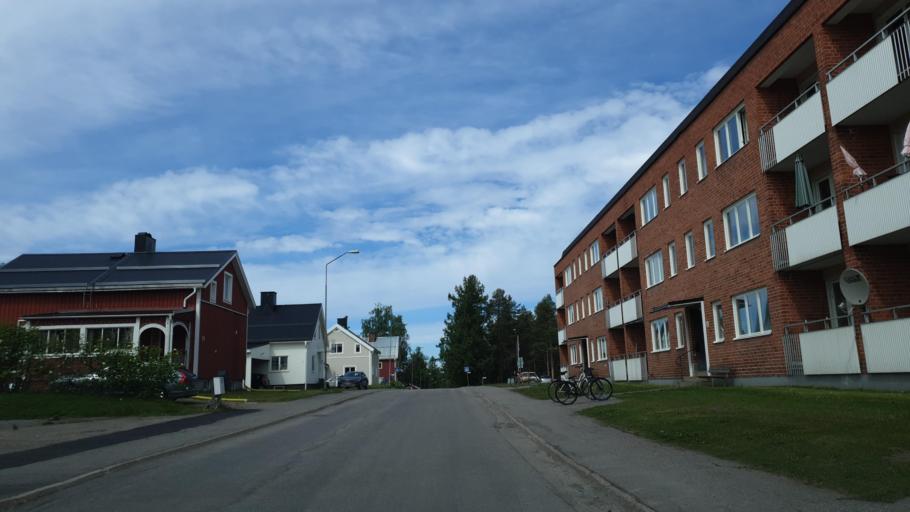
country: SE
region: Norrbotten
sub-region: Arvidsjaurs Kommun
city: Arvidsjaur
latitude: 65.5930
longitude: 19.1804
